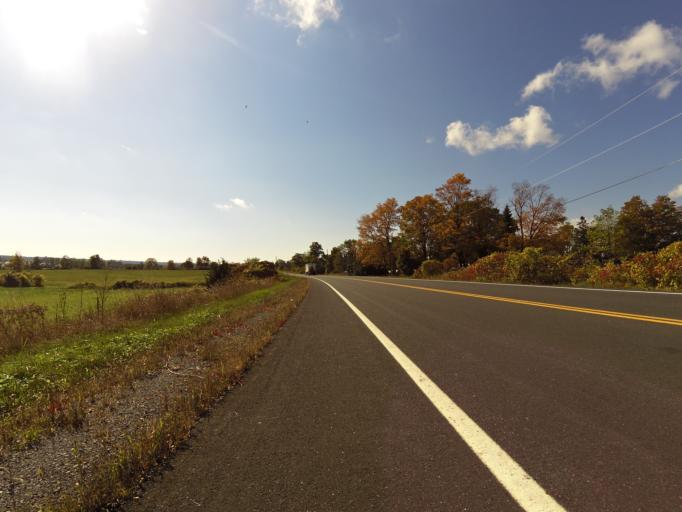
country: CA
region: Ontario
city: Deseronto
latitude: 44.0953
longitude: -76.9464
